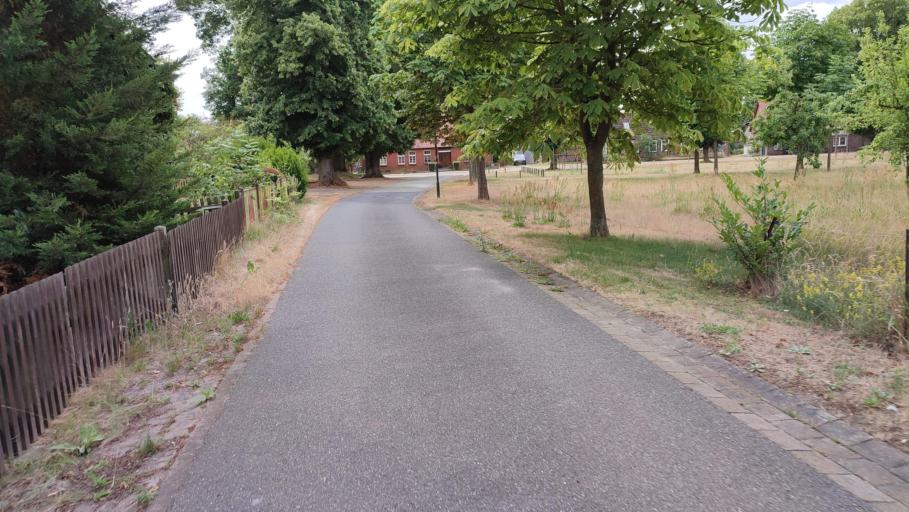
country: DE
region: Lower Saxony
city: Hitzacker
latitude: 53.1840
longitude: 11.1093
